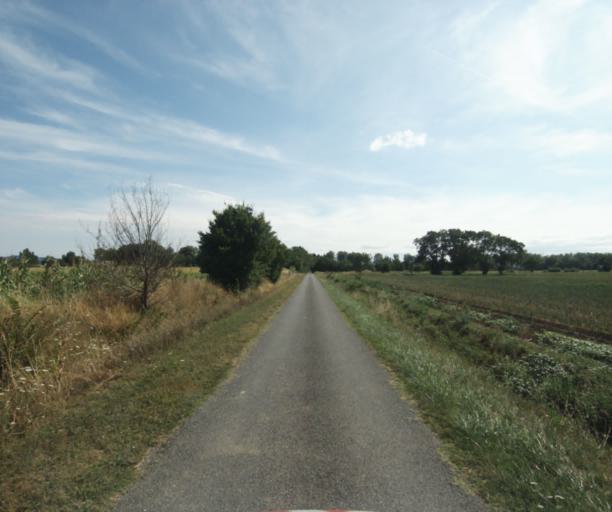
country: FR
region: Midi-Pyrenees
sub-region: Departement de la Haute-Garonne
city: Revel
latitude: 43.5015
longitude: 1.9676
